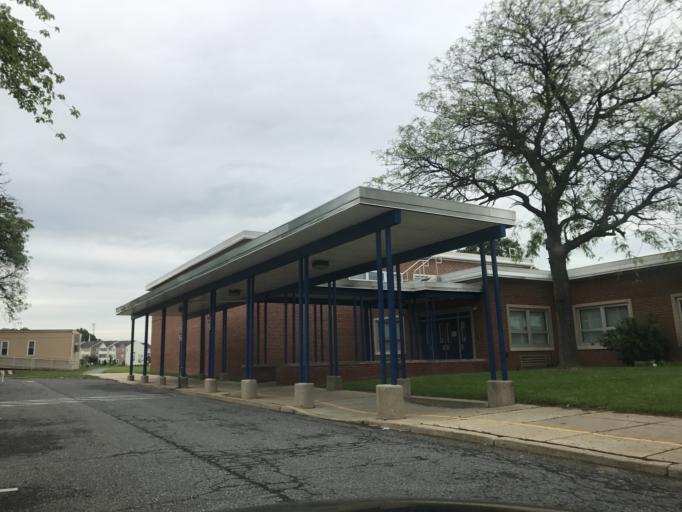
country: US
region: Maryland
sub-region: Baltimore County
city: Middle River
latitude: 39.3460
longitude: -76.4486
